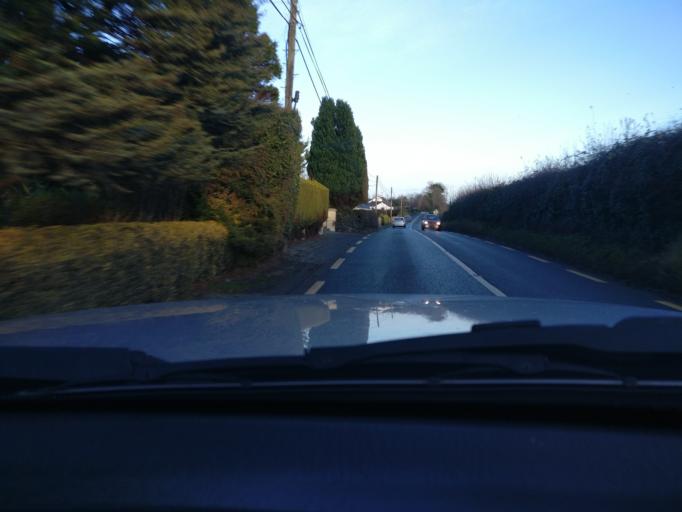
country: IE
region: Leinster
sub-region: Lu
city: Ardee
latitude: 53.8489
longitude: -6.5910
